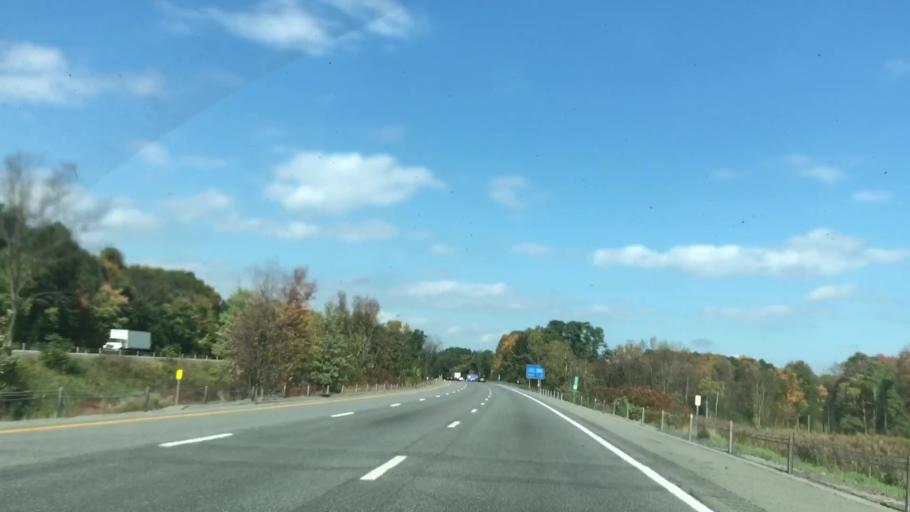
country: US
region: New York
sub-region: Saratoga County
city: Saratoga Springs
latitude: 43.0816
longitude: -73.7481
